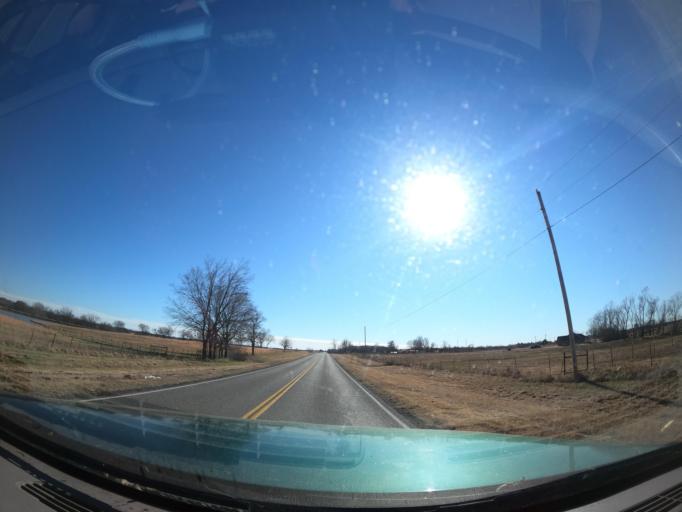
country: US
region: Oklahoma
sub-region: Muskogee County
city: Haskell
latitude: 35.6839
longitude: -95.6423
